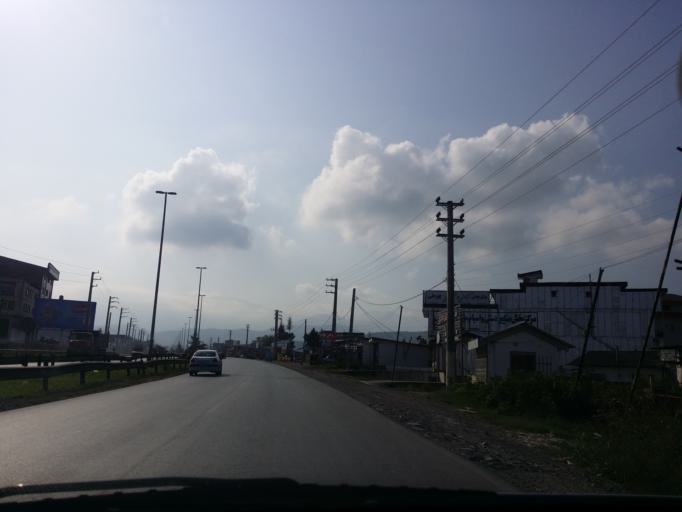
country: IR
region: Mazandaran
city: Chalus
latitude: 36.6708
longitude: 51.3953
